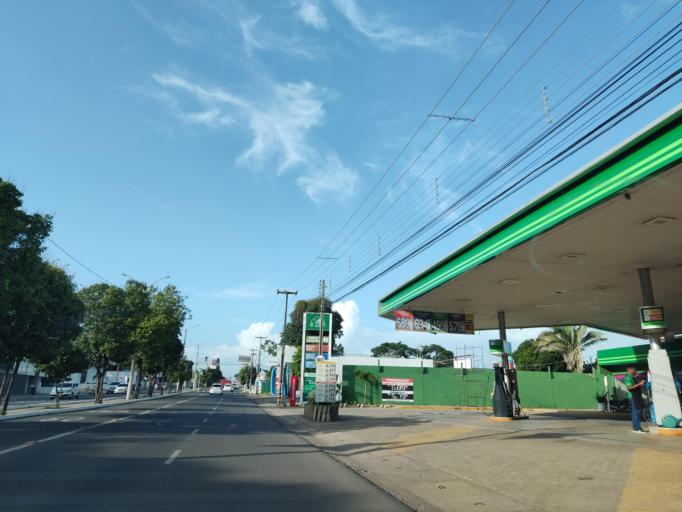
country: BR
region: Piaui
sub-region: Teresina
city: Teresina
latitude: -5.0762
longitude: -42.7734
